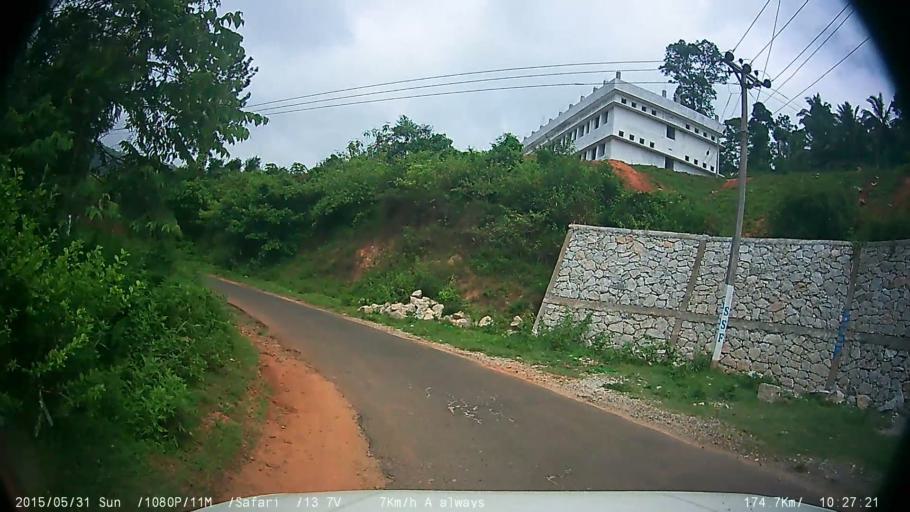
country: IN
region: Kerala
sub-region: Wayanad
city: Kalpetta
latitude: 11.5261
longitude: 76.1389
